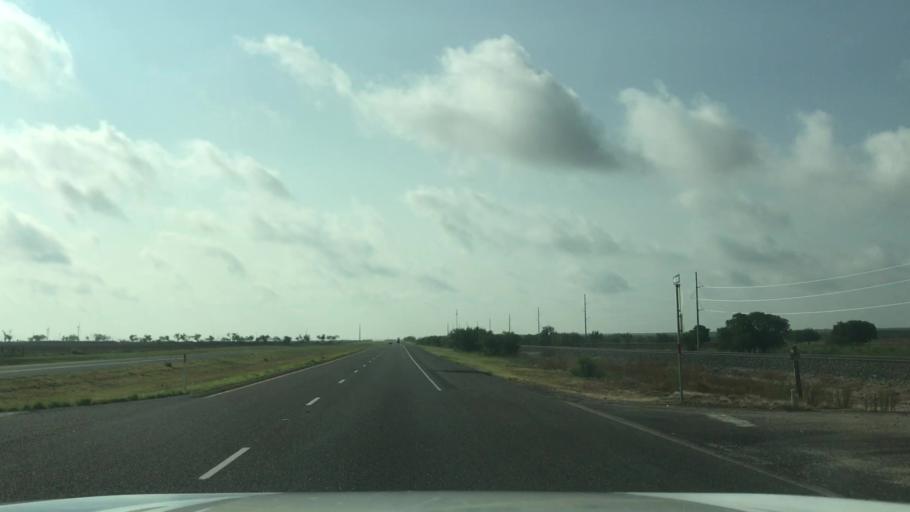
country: US
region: Texas
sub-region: Scurry County
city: Snyder
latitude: 32.8732
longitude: -101.0421
